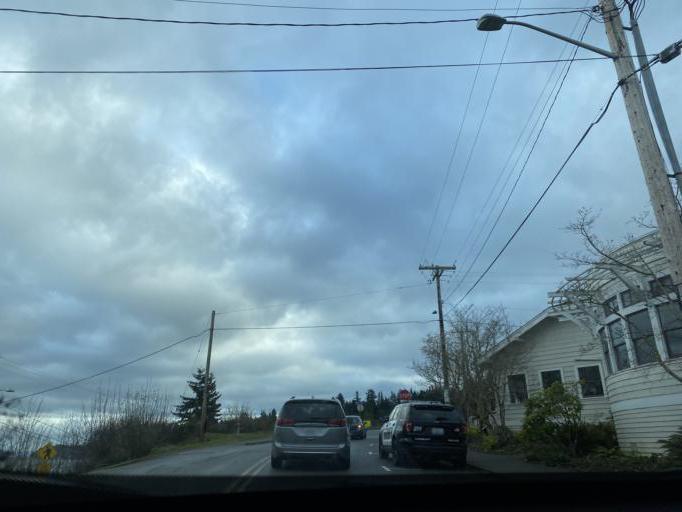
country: US
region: Washington
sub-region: Island County
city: Langley
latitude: 48.0403
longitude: -122.4065
